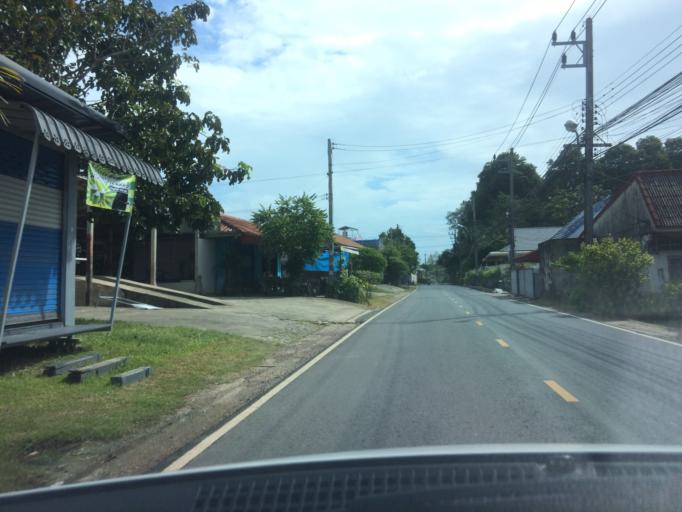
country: TH
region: Phuket
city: Thalang
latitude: 8.0286
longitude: 98.3375
